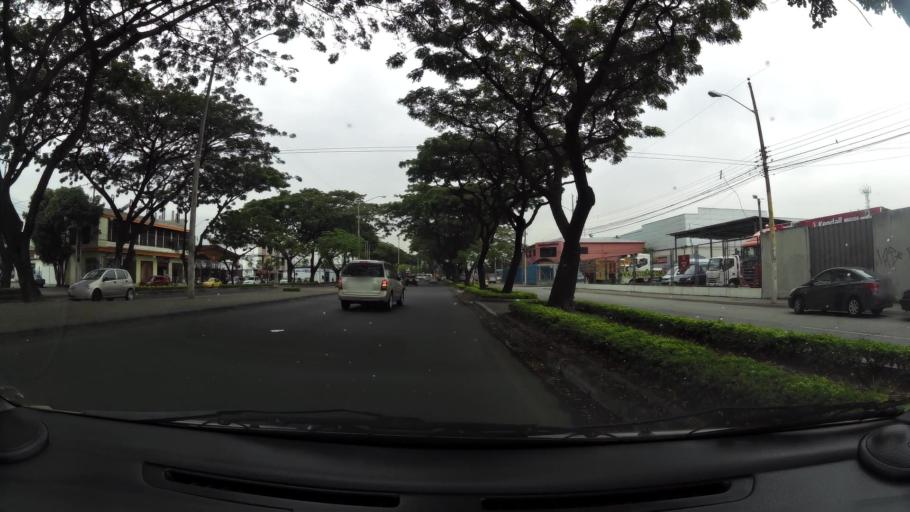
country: EC
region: Guayas
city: Eloy Alfaro
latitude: -2.1436
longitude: -79.8874
